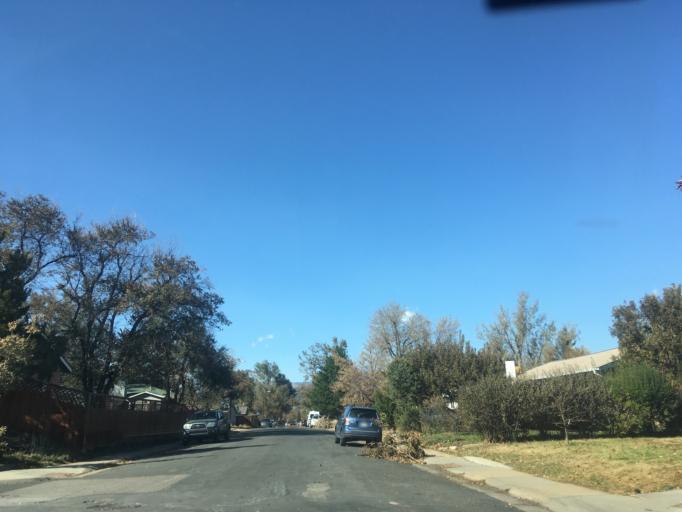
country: US
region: Colorado
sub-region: Boulder County
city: Boulder
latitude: 39.9893
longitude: -105.2452
